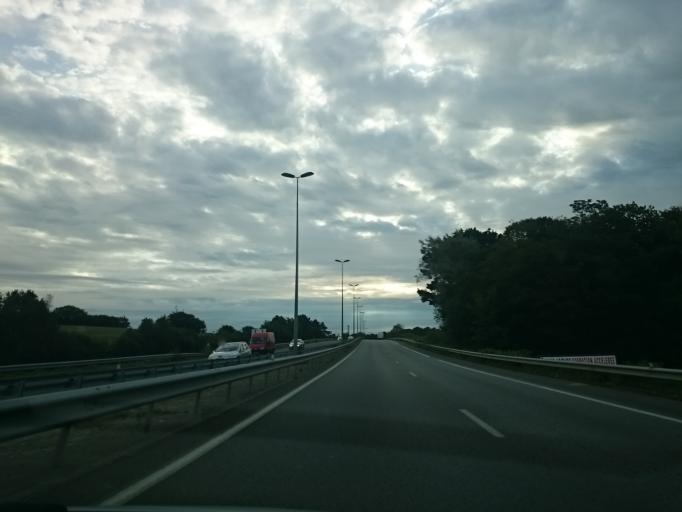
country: FR
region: Brittany
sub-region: Departement du Finistere
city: Guipavas
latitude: 48.4182
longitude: -4.4348
